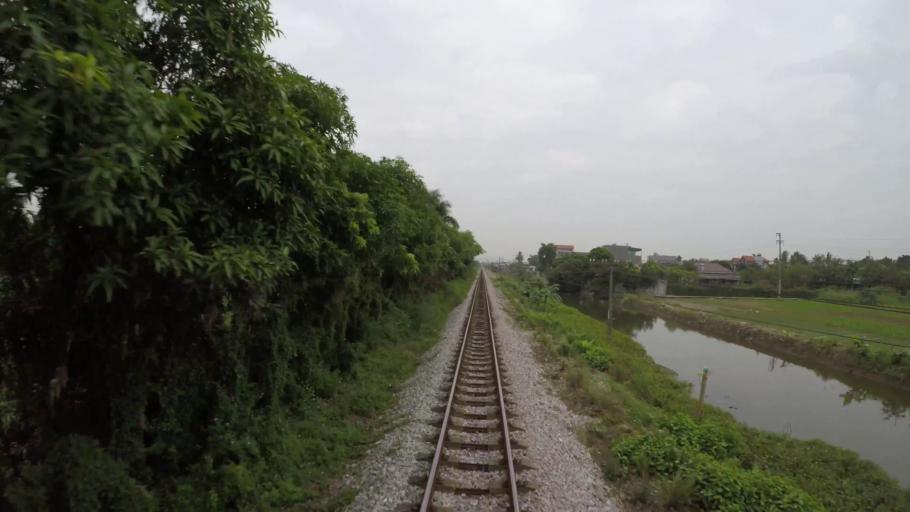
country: VN
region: Hai Phong
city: An Duong
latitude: 20.8911
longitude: 106.5932
